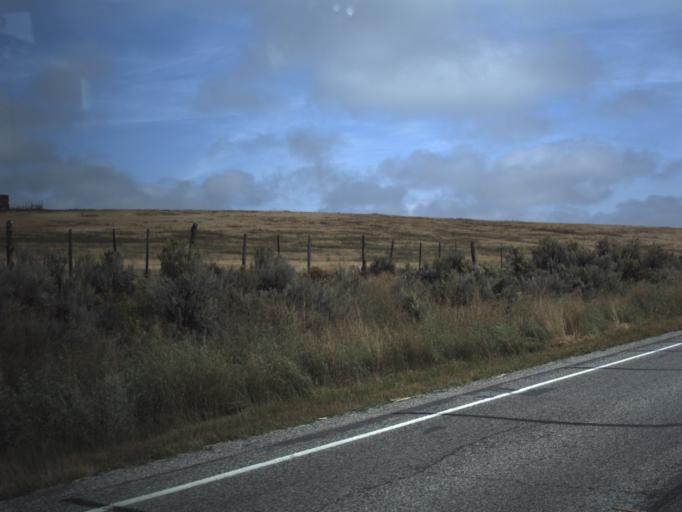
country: US
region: Utah
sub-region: Rich County
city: Randolph
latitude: 41.6989
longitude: -111.1669
